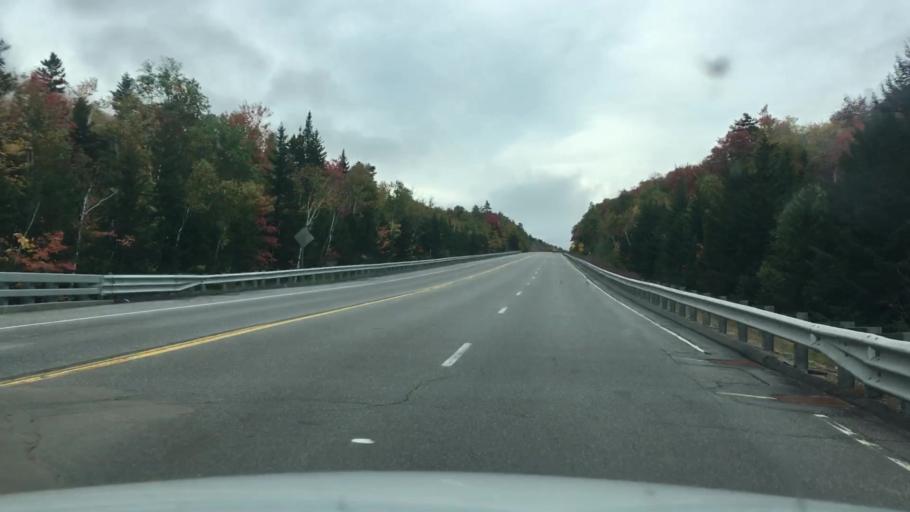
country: US
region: New Hampshire
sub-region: Coos County
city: Gorham
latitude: 44.2710
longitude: -71.2353
